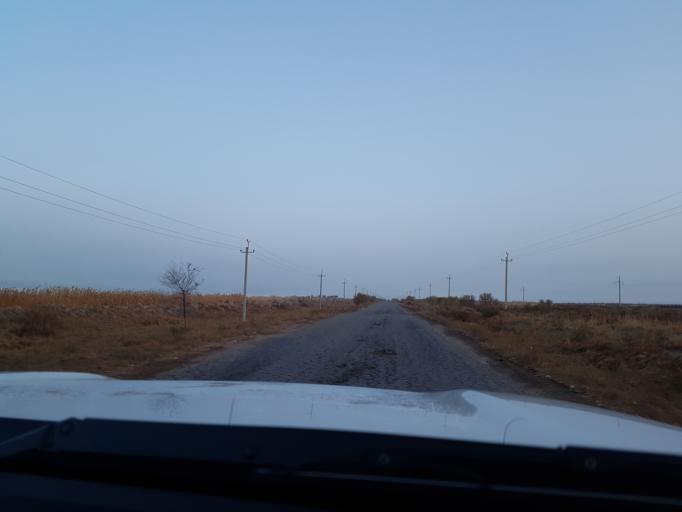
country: TM
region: Dasoguz
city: Koeneuergench
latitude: 41.7751
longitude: 58.6951
